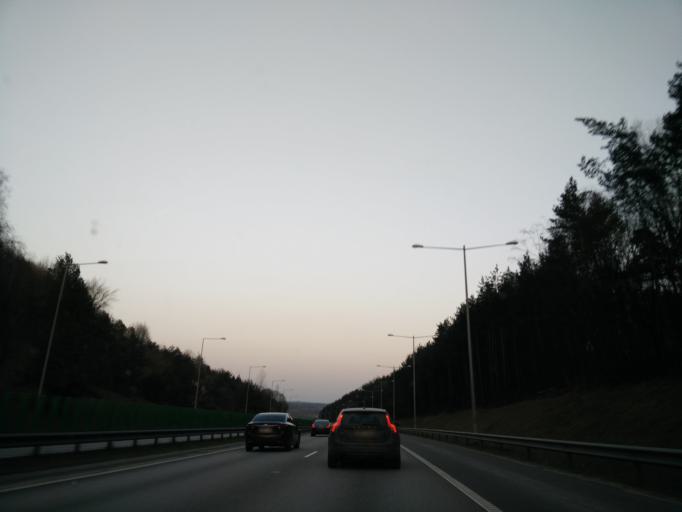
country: LT
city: Grigiskes
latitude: 54.6801
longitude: 25.0641
